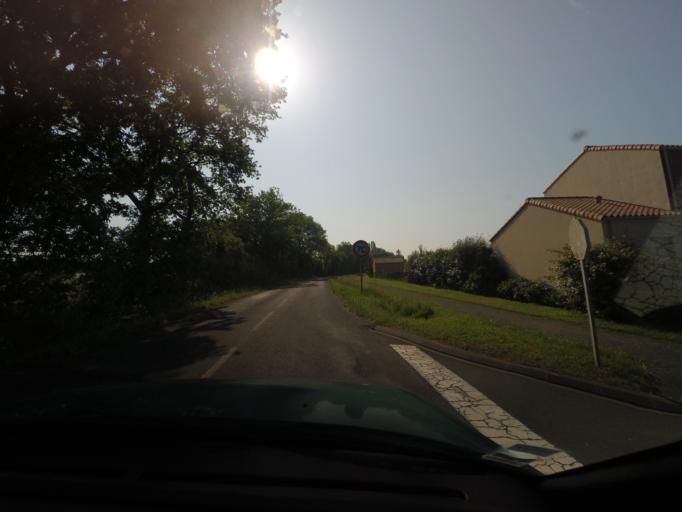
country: FR
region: Pays de la Loire
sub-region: Departement de la Loire-Atlantique
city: Mouzillon
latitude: 47.1448
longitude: -1.2911
